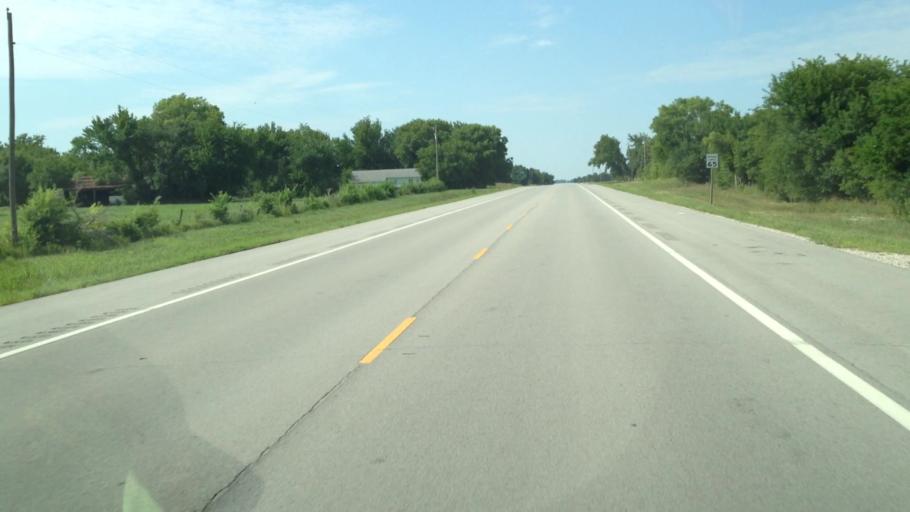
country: US
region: Kansas
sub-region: Labette County
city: Altamont
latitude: 37.2537
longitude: -95.2671
